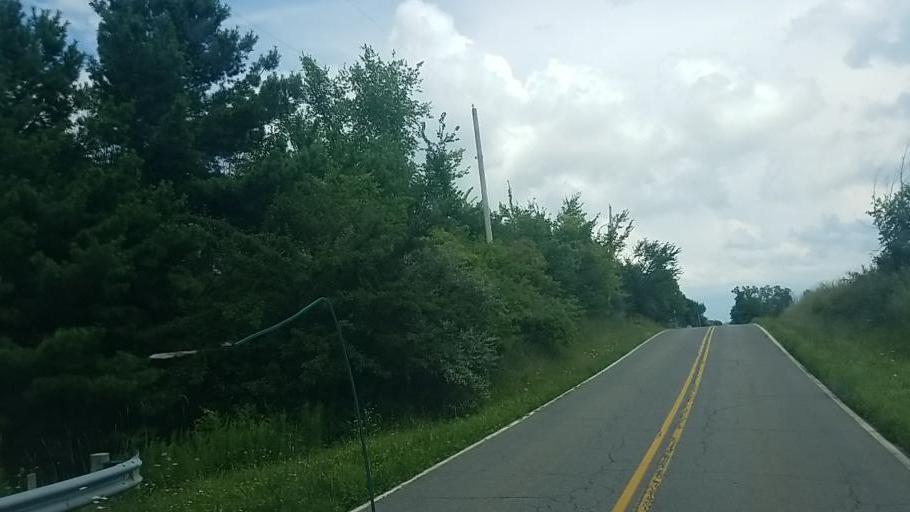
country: US
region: Ohio
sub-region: Medina County
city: Medina
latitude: 41.1423
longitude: -81.9665
